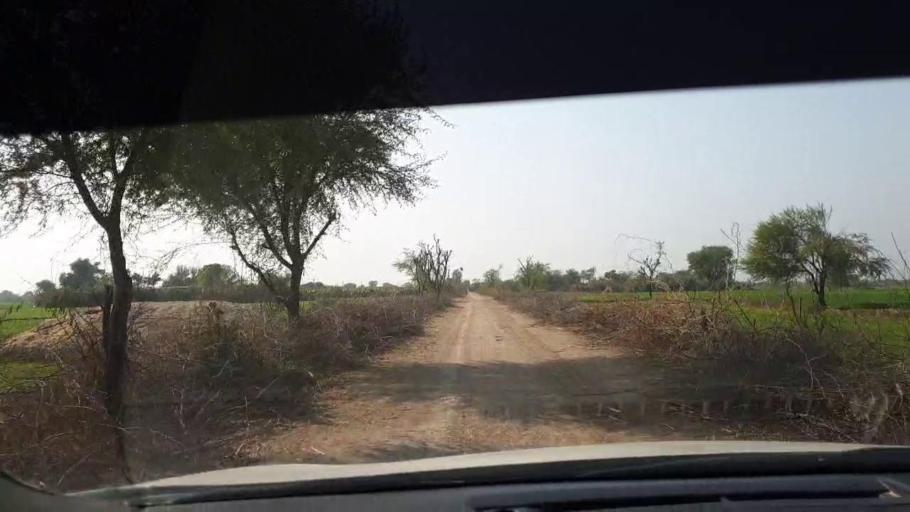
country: PK
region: Sindh
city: Tando Adam
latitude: 25.8403
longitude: 68.7175
